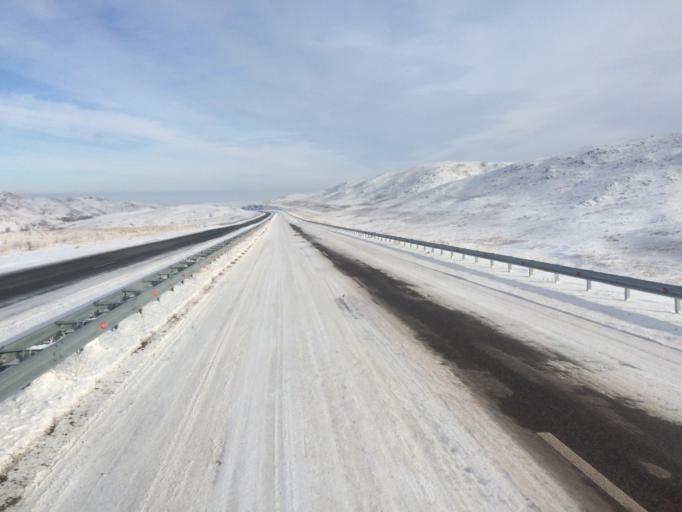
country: KZ
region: Zhambyl
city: Georgiyevka
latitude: 43.4282
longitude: 74.8952
